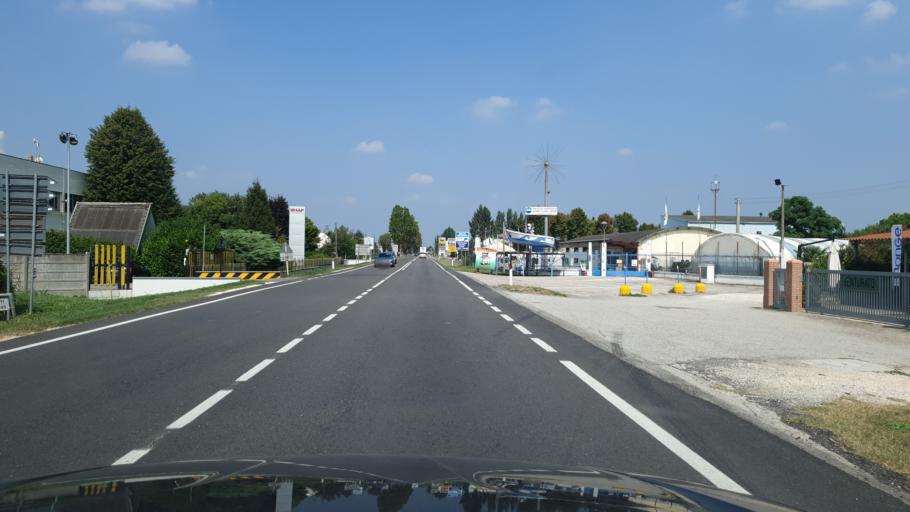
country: IT
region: Veneto
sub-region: Provincia di Rovigo
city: Bosaro
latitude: 45.0082
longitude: 11.7655
